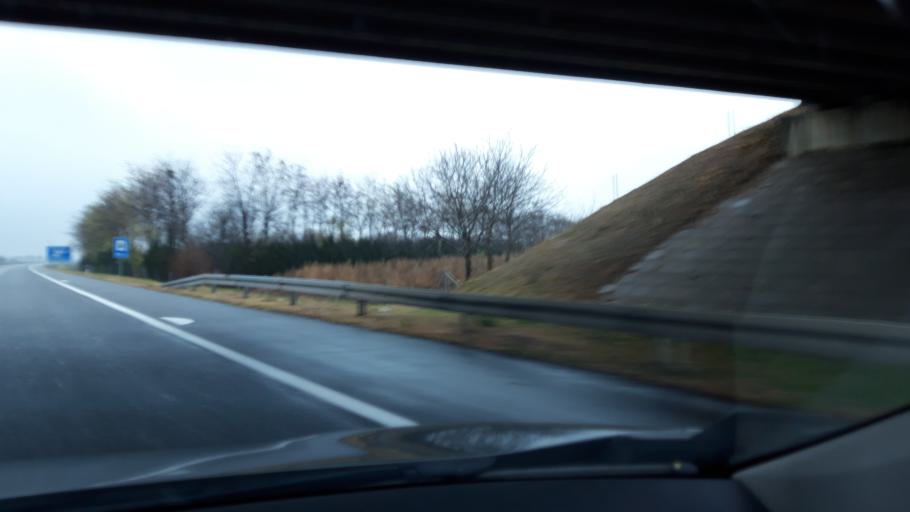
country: HU
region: Csongrad
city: Asotthalom
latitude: 46.0844
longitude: 19.7873
